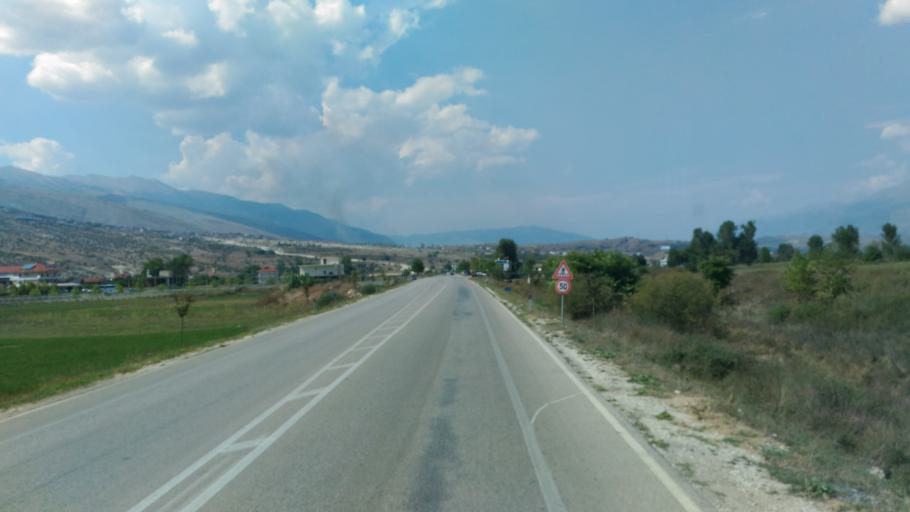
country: AL
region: Gjirokaster
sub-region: Rrethi i Gjirokastres
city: Dervician
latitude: 40.0323
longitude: 20.1835
